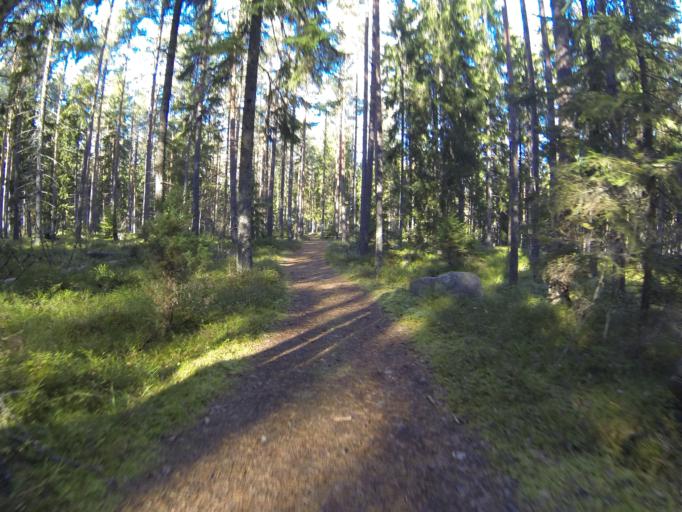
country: FI
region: Varsinais-Suomi
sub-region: Salo
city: Saerkisalo
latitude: 60.2073
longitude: 22.9222
